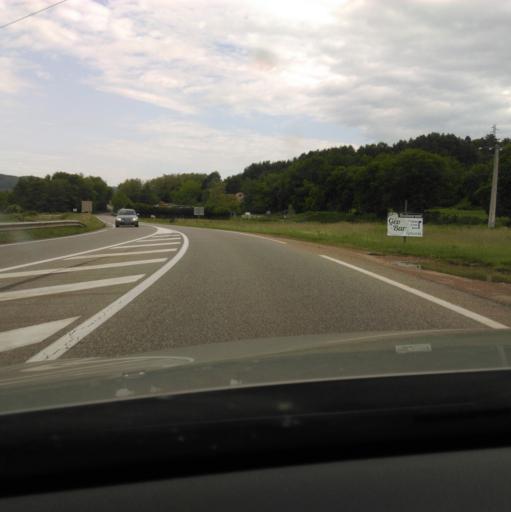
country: FR
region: Rhone-Alpes
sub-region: Departement de l'Ain
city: Montreal-la-Cluse
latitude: 46.1801
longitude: 5.5498
